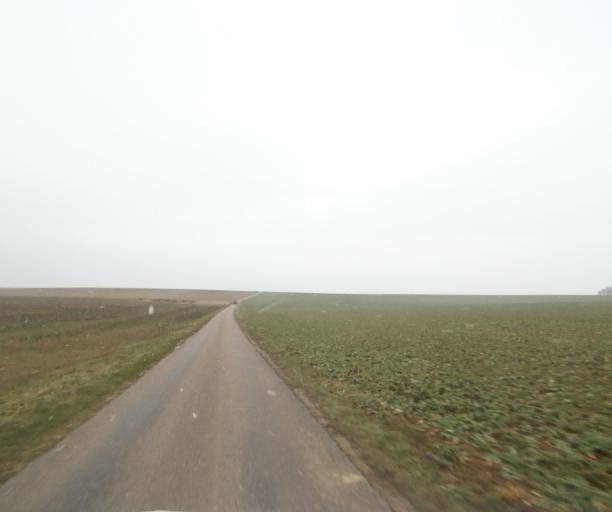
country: FR
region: Champagne-Ardenne
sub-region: Departement de la Haute-Marne
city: Chevillon
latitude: 48.5117
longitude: 5.0865
